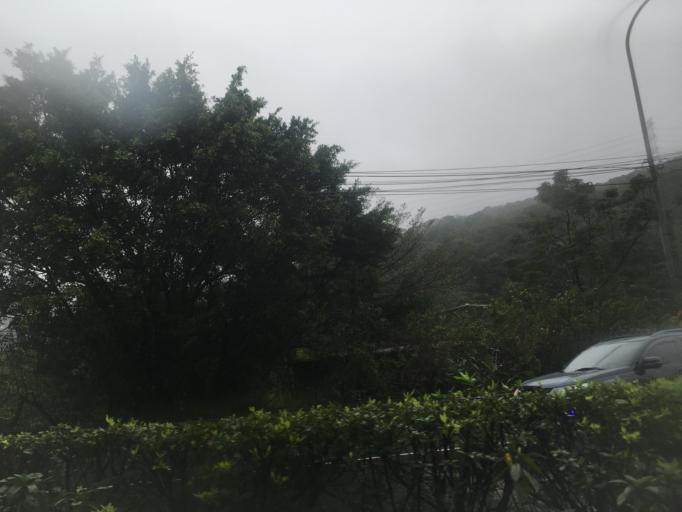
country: TW
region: Taiwan
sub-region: Keelung
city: Keelung
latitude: 25.1126
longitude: 121.6906
